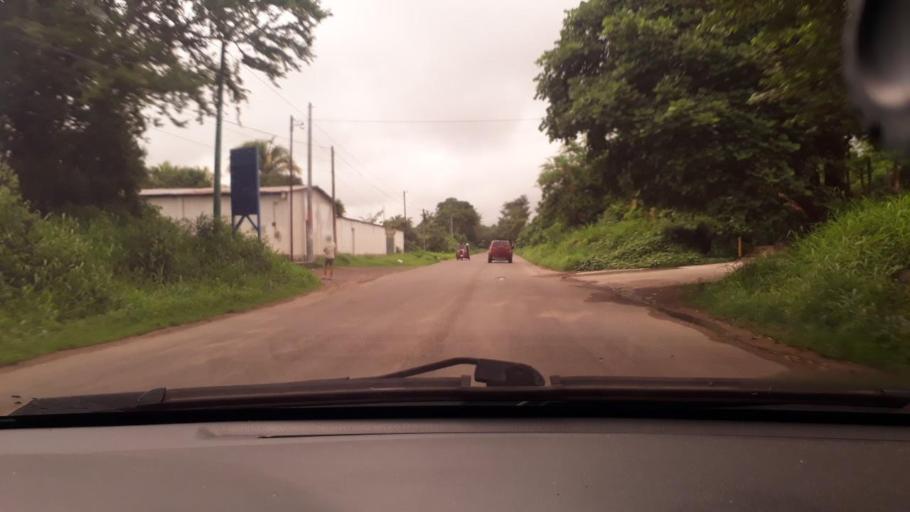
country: GT
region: Jutiapa
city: Jalpatagua
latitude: 14.1538
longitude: -90.0456
